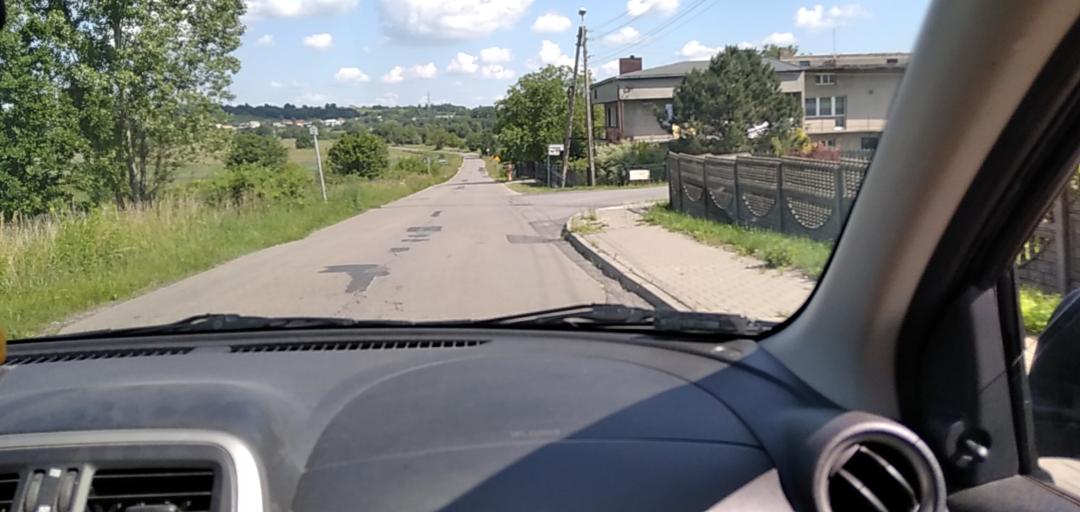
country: PL
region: Silesian Voivodeship
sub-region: Powiat bedzinski
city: Sarnow
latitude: 50.3922
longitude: 19.1395
